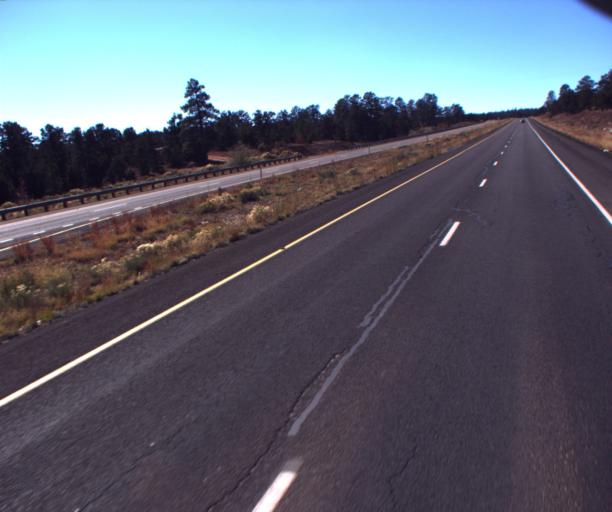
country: US
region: Arizona
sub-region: Apache County
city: Saint Michaels
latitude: 35.6576
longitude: -109.1390
